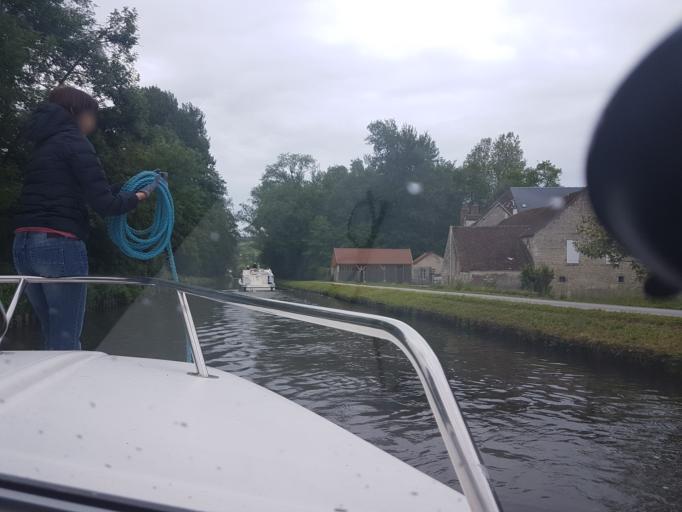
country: FR
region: Bourgogne
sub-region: Departement de l'Yonne
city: Champs-sur-Yonne
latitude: 47.7239
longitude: 3.6180
